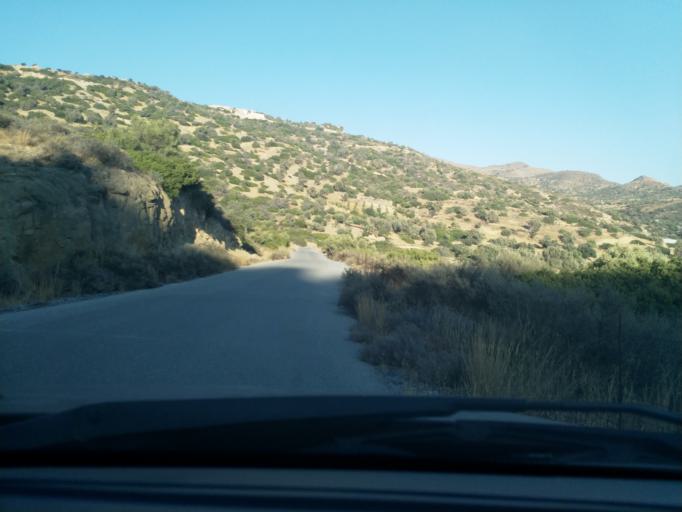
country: GR
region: Crete
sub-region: Nomos Rethymnis
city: Agia Galini
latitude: 35.1193
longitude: 24.5585
